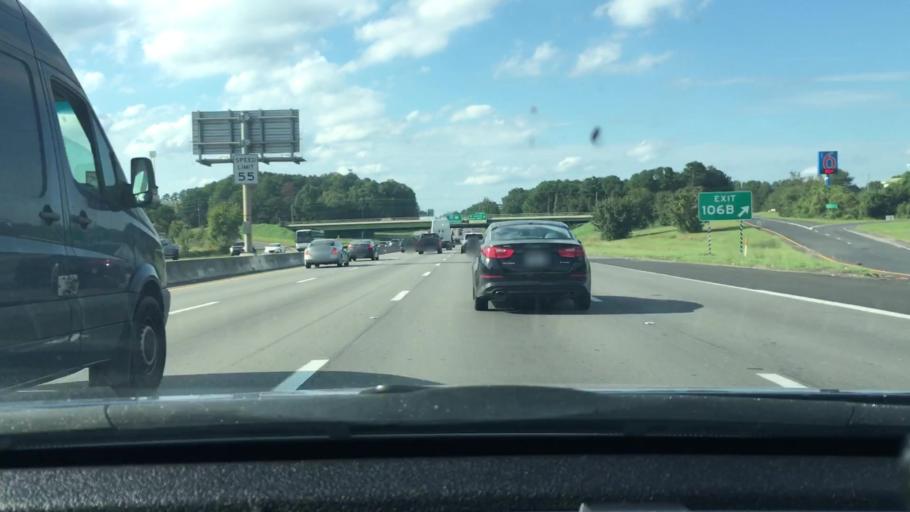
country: US
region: South Carolina
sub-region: Lexington County
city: Saint Andrews
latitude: 34.0426
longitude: -81.1159
